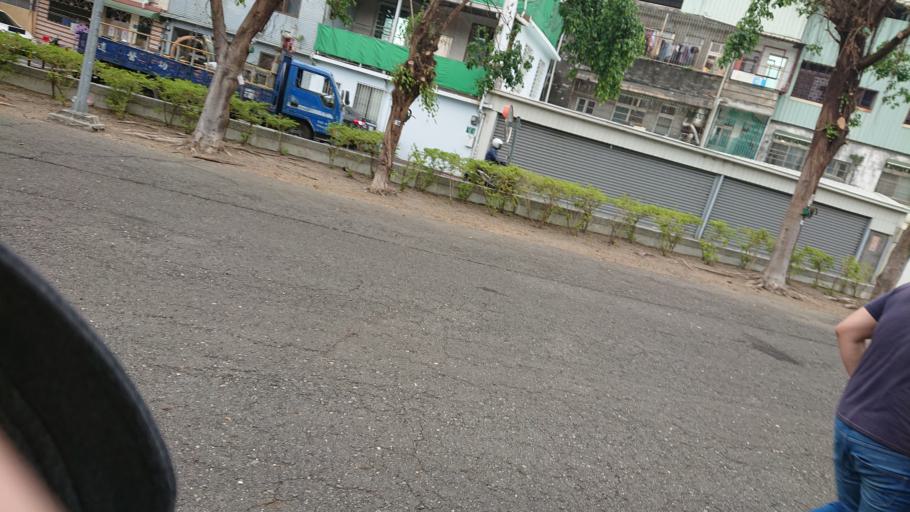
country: TW
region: Kaohsiung
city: Kaohsiung
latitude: 22.7050
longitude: 120.2935
